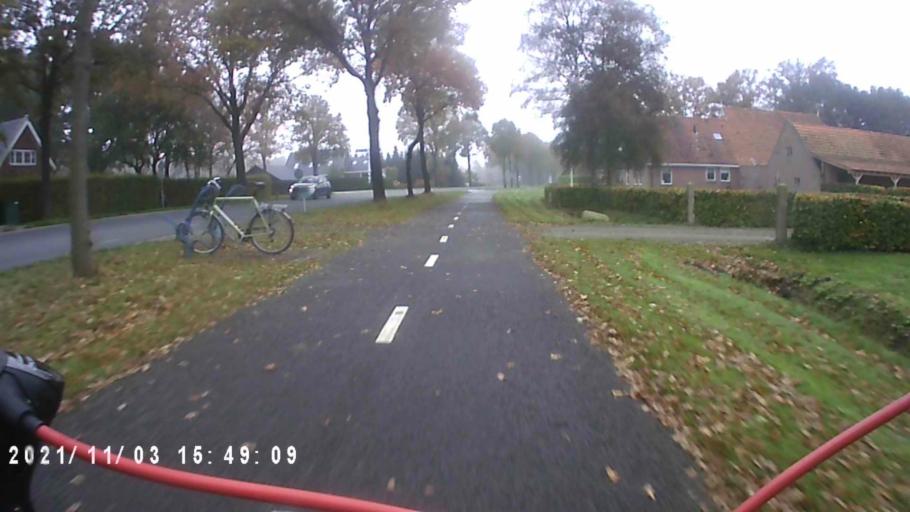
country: NL
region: Groningen
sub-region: Gemeente Leek
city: Leek
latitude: 53.0850
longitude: 6.3384
